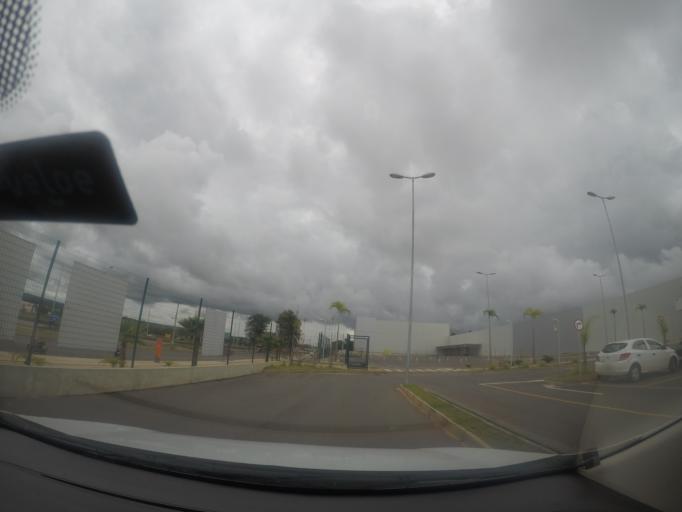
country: BR
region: Goias
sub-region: Trindade
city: Trindade
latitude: -16.6553
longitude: -49.3842
